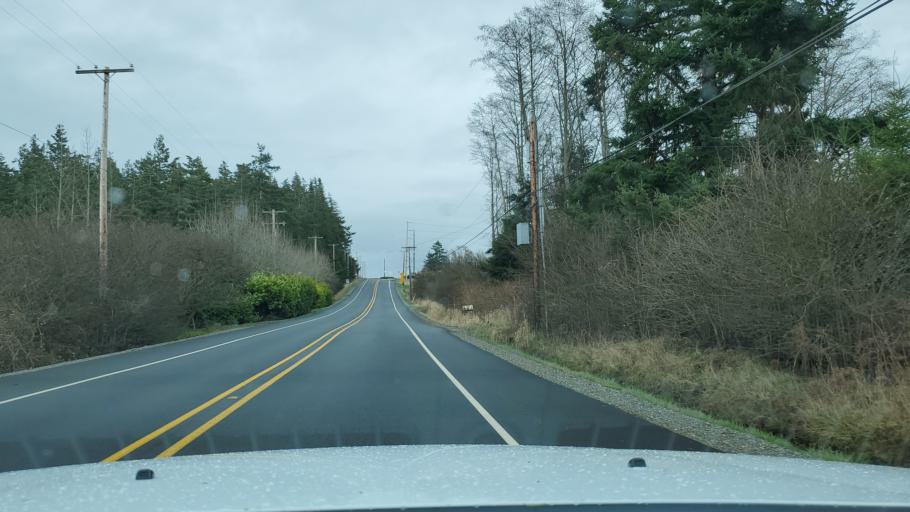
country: US
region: Washington
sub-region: Island County
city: Ault Field
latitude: 48.3259
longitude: -122.6781
